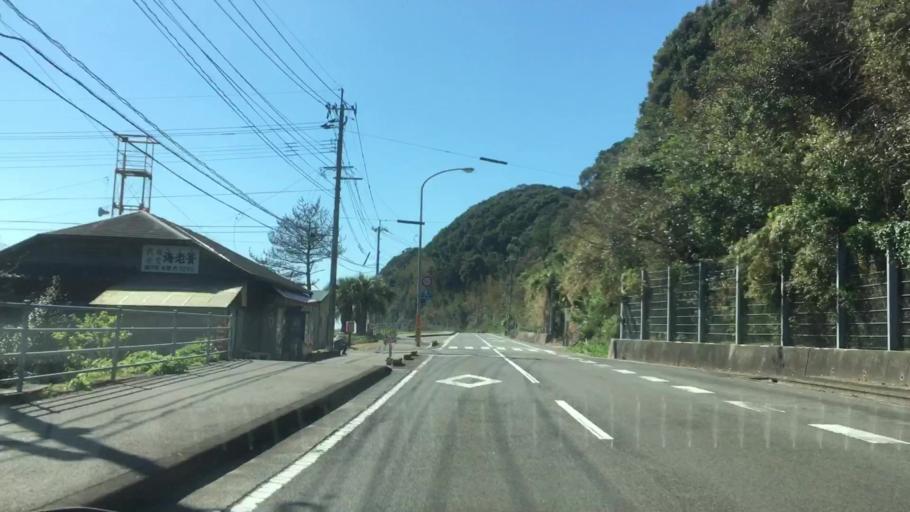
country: JP
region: Nagasaki
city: Sasebo
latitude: 33.0292
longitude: 129.6023
